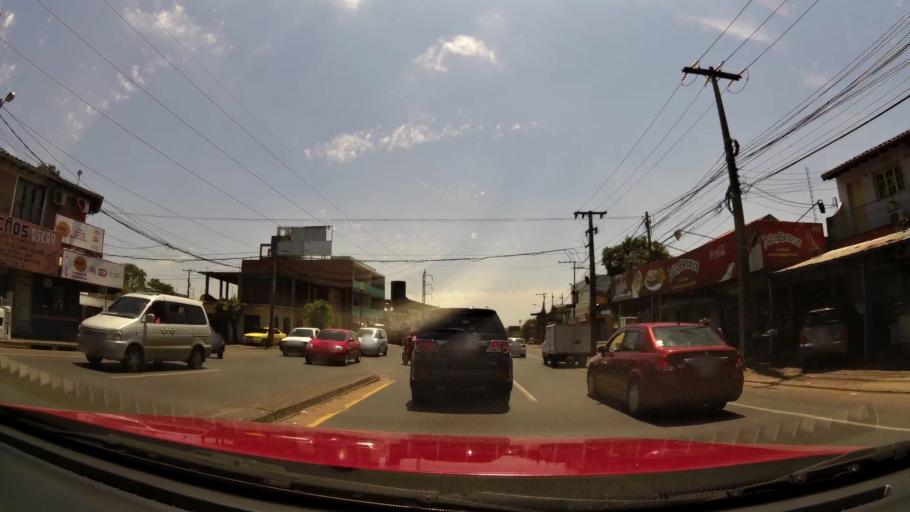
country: PY
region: Central
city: Lambare
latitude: -25.3442
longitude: -57.5808
